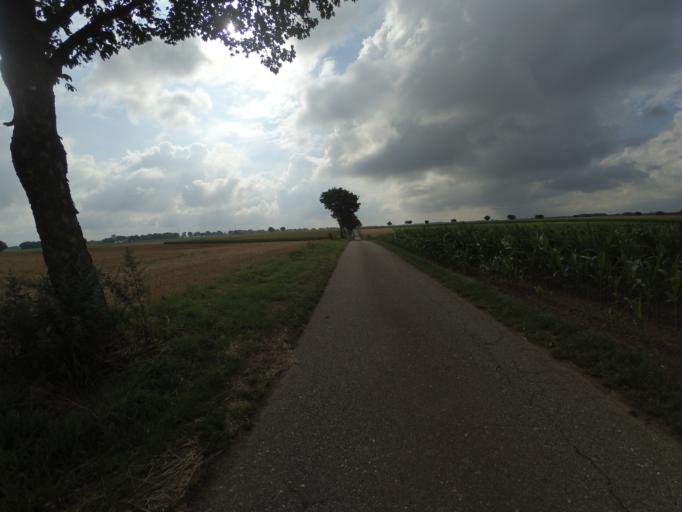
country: DE
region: North Rhine-Westphalia
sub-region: Regierungsbezirk Koln
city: Selfkant
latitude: 51.0477
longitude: 5.9171
